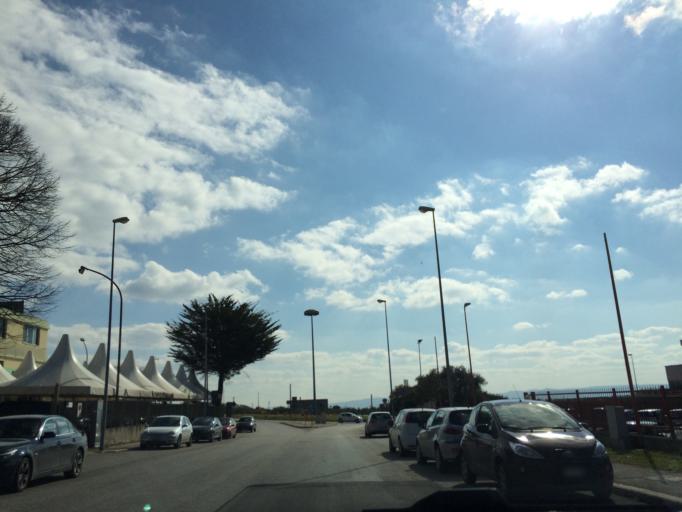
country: IT
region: Basilicate
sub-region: Provincia di Matera
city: Matera
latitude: 40.6699
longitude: 16.5736
